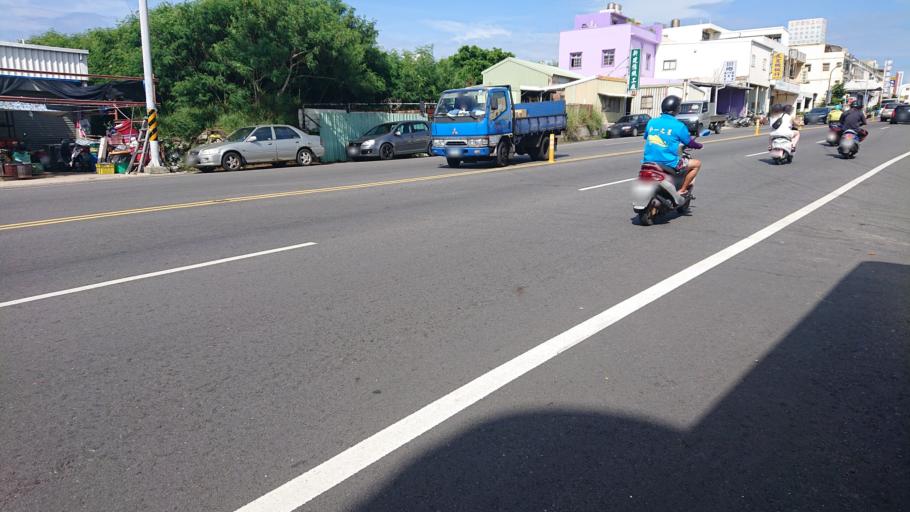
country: TW
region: Taiwan
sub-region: Penghu
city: Ma-kung
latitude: 23.5642
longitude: 119.5884
